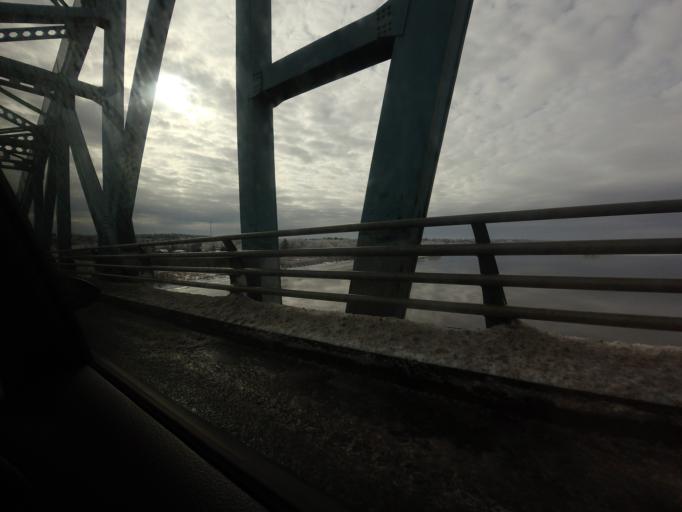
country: CA
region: New Brunswick
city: Oromocto
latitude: 45.8640
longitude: -66.4507
